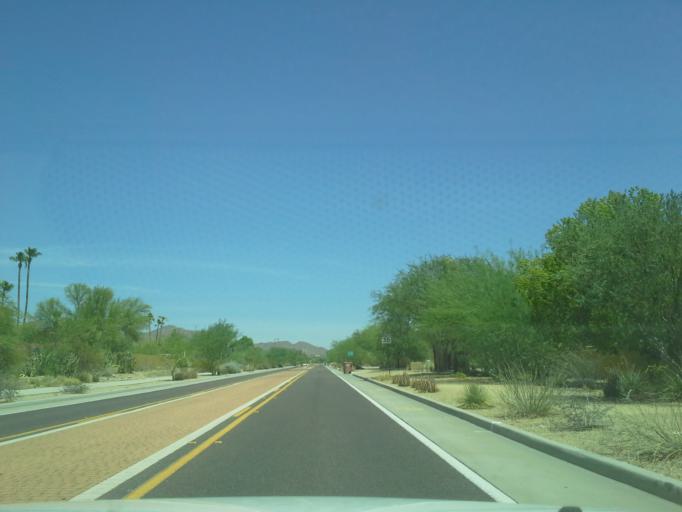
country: US
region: Arizona
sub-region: Maricopa County
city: Scottsdale
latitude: 33.5969
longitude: -111.8551
